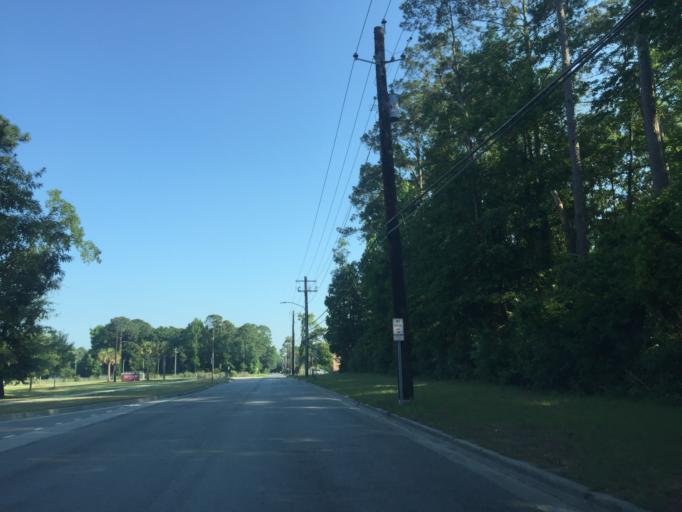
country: US
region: Georgia
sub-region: Chatham County
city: Isle of Hope
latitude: 31.9960
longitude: -81.0777
